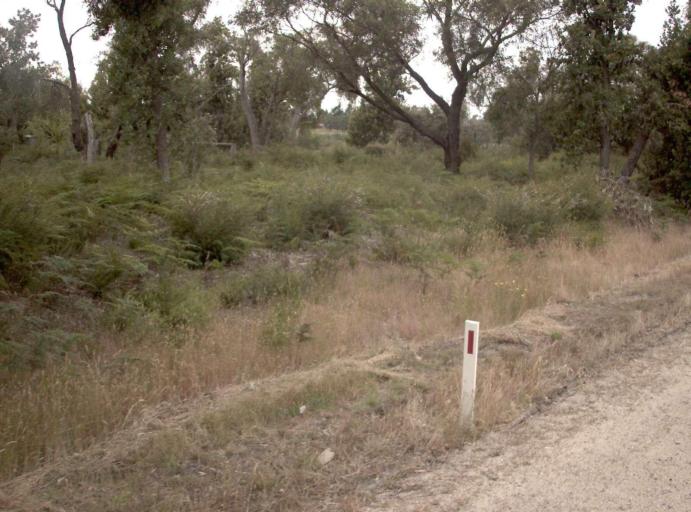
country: AU
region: Victoria
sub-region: Wellington
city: Sale
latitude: -38.1819
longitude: 147.1365
